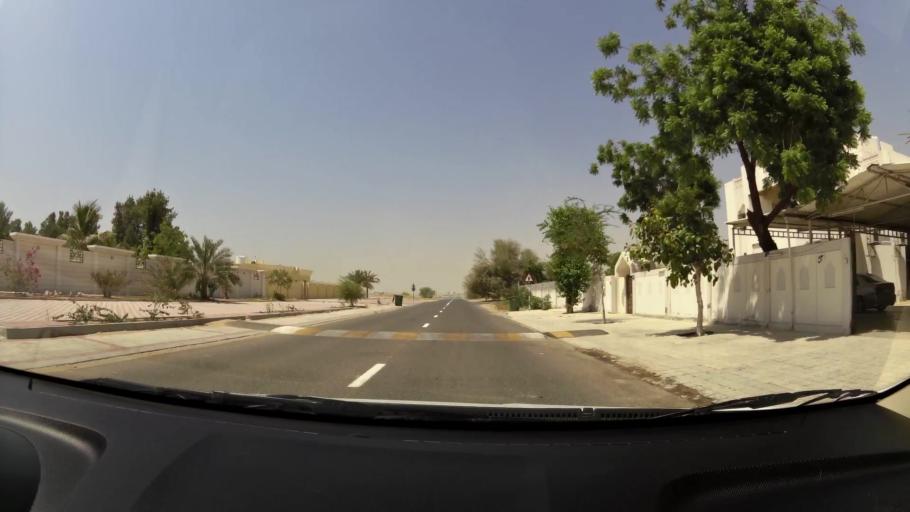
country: AE
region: Ajman
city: Ajman
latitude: 25.4275
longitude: 55.5038
